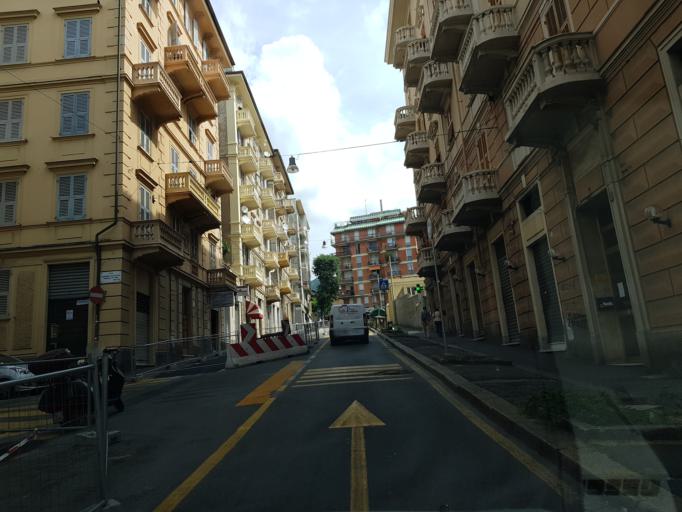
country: IT
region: Liguria
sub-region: Provincia di Genova
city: San Teodoro
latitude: 44.4280
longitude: 8.8513
